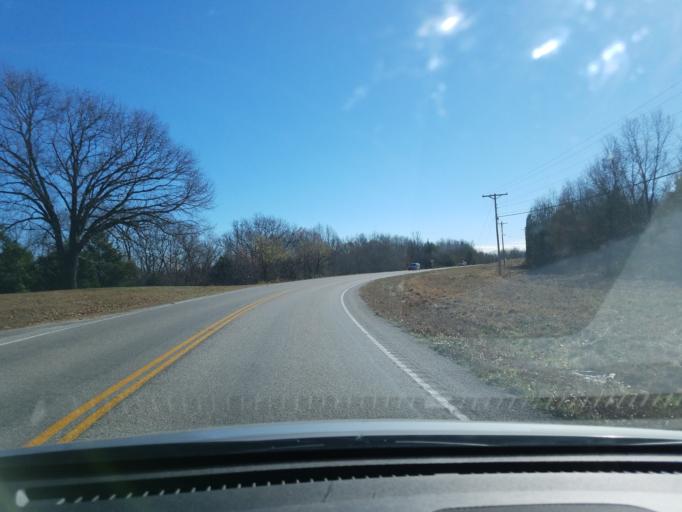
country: US
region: Missouri
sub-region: Taney County
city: Hollister
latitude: 36.5262
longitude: -93.2767
